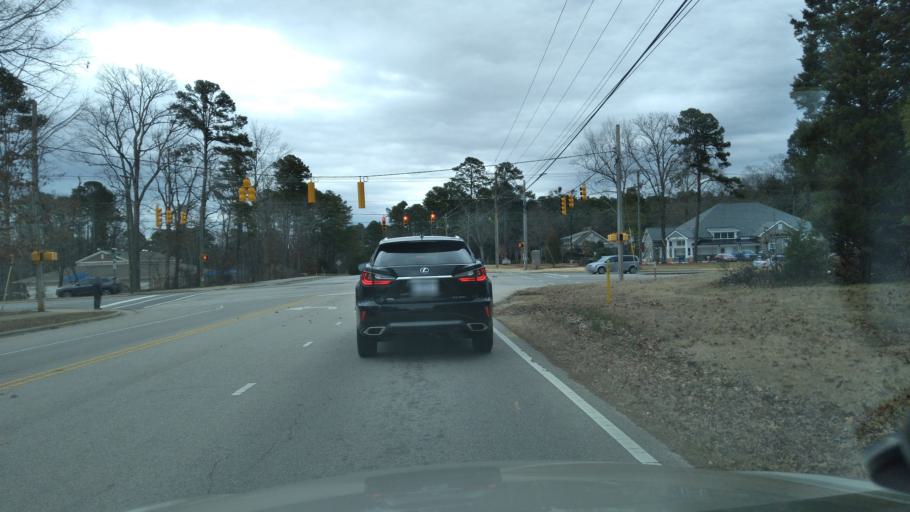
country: US
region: North Carolina
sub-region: Wake County
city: Apex
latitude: 35.7339
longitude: -78.8407
